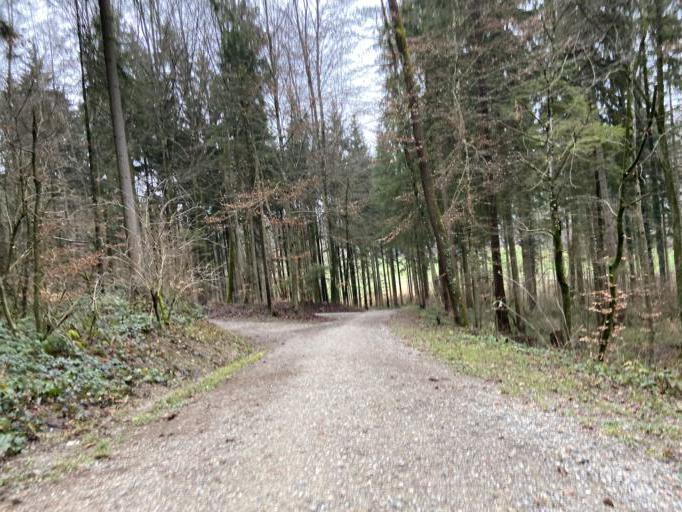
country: CH
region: Zurich
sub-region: Bezirk Winterthur
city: Toess (Kreis 4) / Vorder-Daettnau
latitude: 47.4889
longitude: 8.6846
